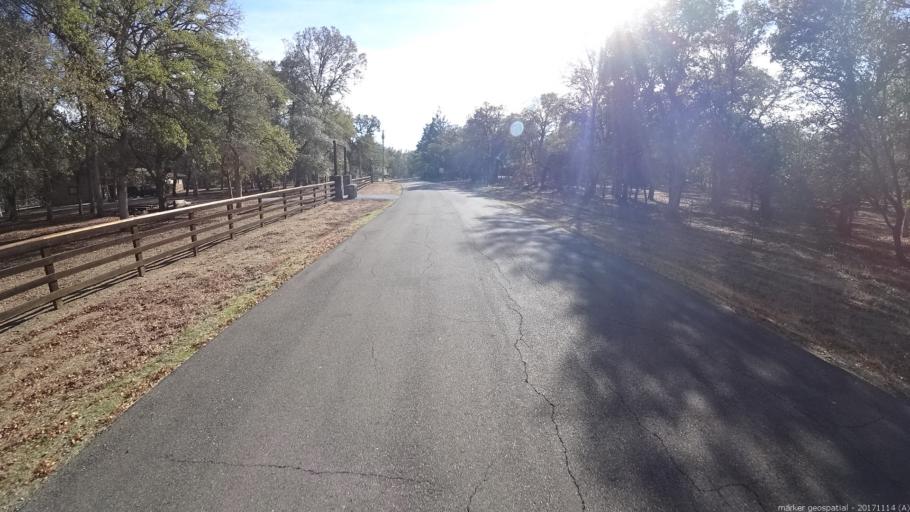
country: US
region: California
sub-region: Shasta County
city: Anderson
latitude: 40.3829
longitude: -122.4471
